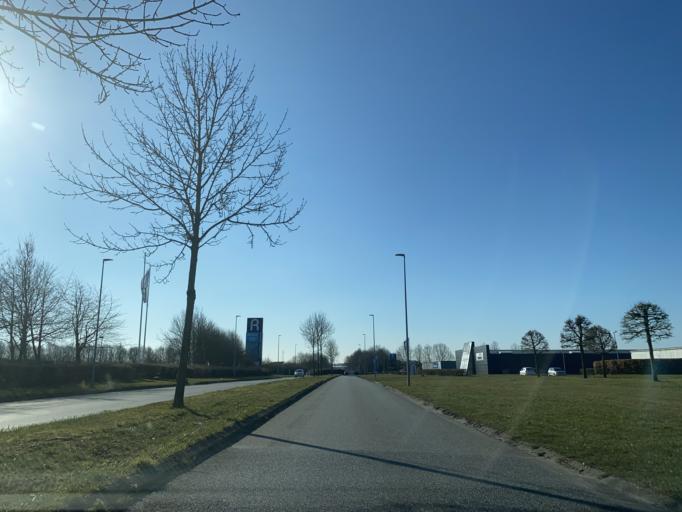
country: DK
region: Central Jutland
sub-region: Randers Kommune
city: Randers
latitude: 56.4299
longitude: 10.0611
